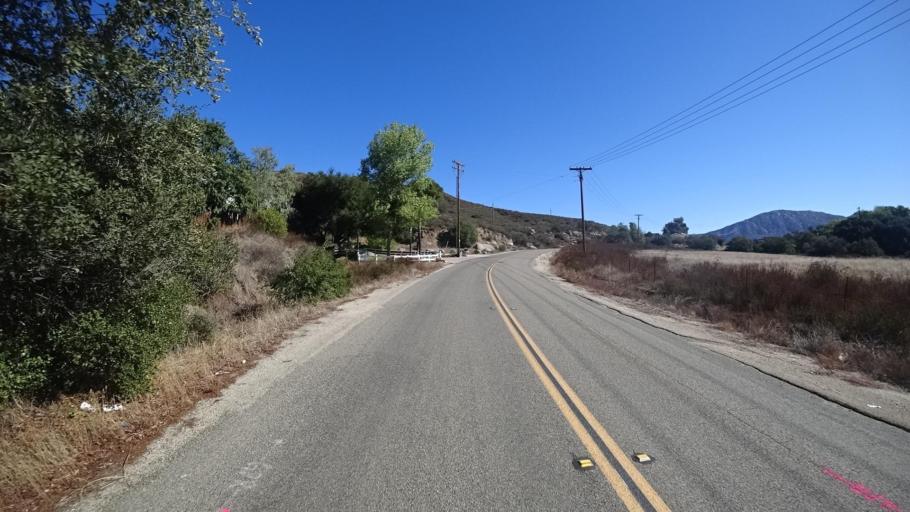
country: US
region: California
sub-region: San Diego County
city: Alpine
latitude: 32.8395
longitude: -116.7167
